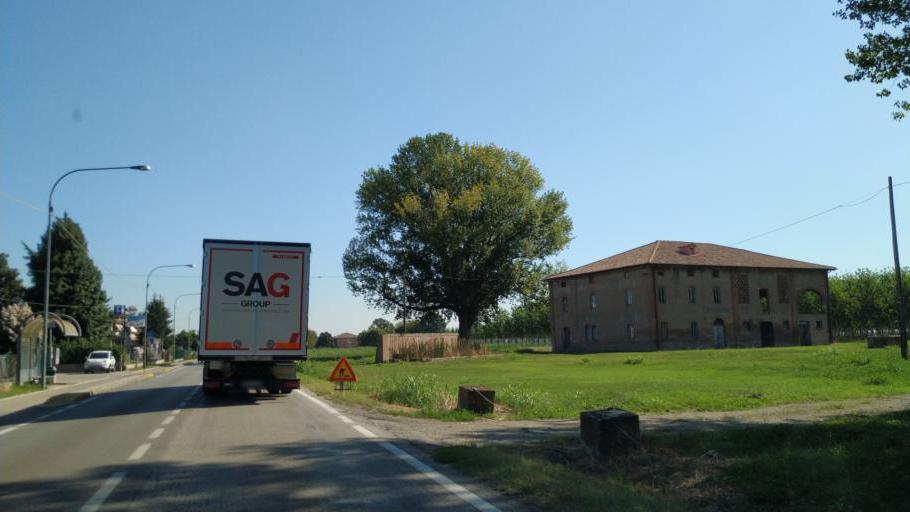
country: IT
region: Emilia-Romagna
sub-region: Provincia di Ferrara
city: Mirabello
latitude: 44.8177
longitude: 11.4488
